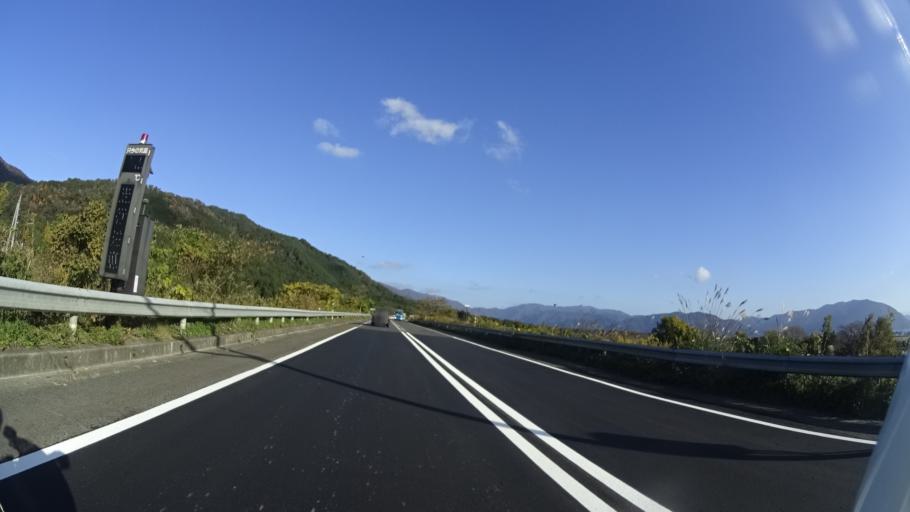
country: JP
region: Fukui
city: Tsuruga
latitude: 35.4313
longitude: 136.0163
